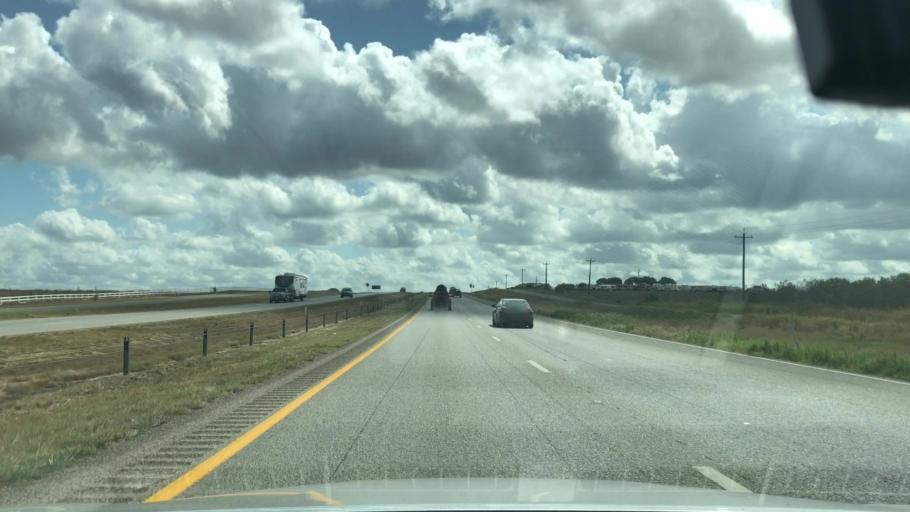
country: US
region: Texas
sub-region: Guadalupe County
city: Marion
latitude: 29.5298
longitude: -98.1093
